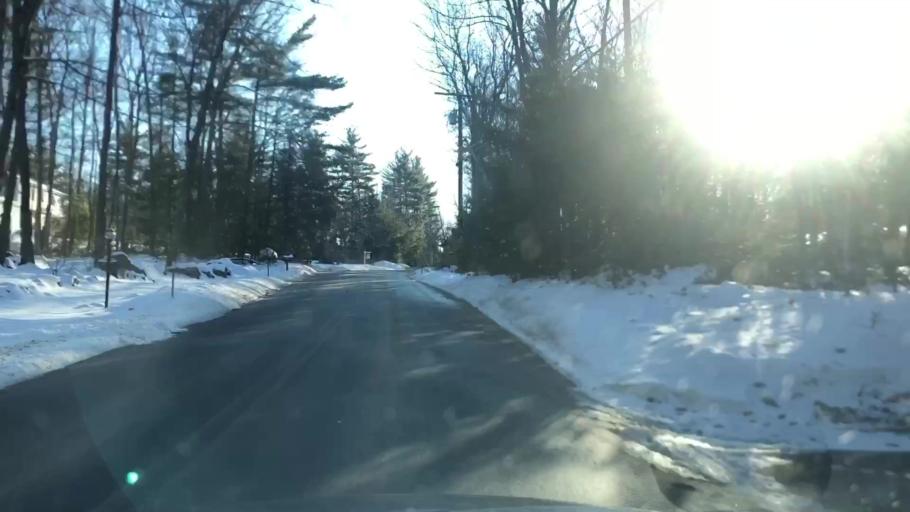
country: US
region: New Hampshire
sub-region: Hillsborough County
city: Milford
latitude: 42.8043
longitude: -71.6689
